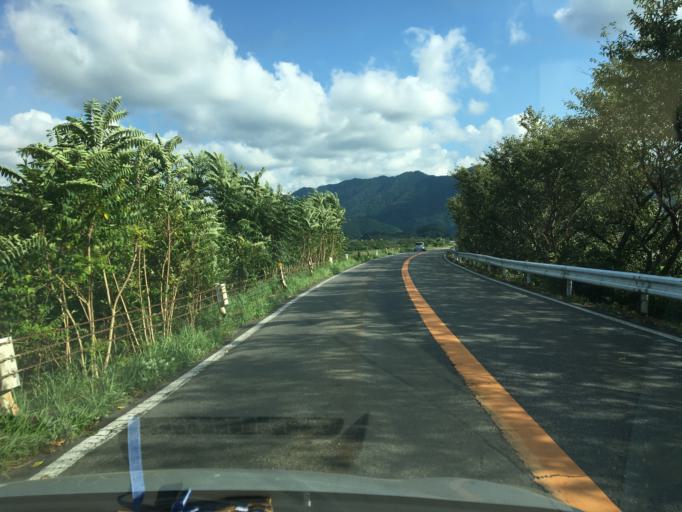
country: JP
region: Hyogo
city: Toyooka
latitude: 35.4387
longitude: 134.7880
